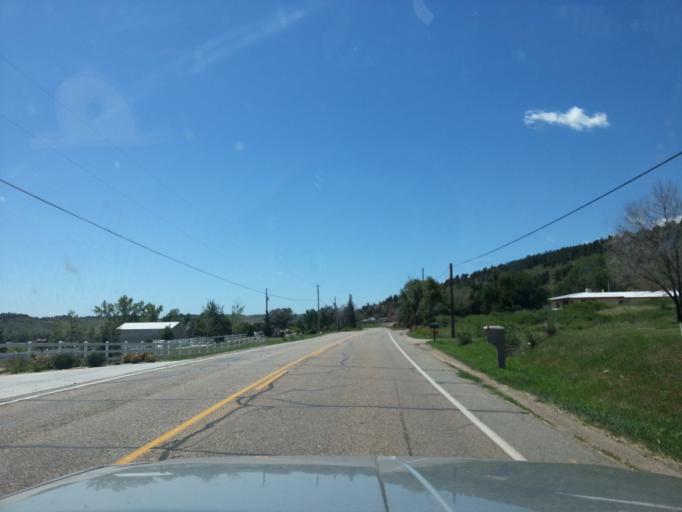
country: US
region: Colorado
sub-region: Larimer County
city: Loveland
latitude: 40.4288
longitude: -105.1930
